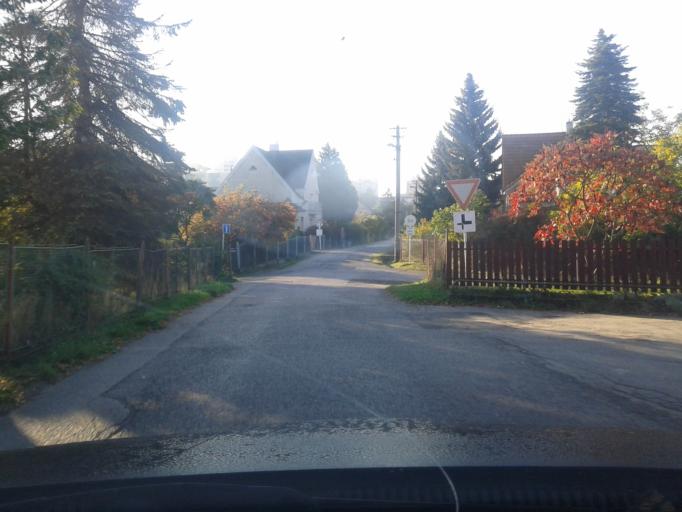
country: CZ
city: Dolni Lutyne
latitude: 49.8792
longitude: 18.4252
